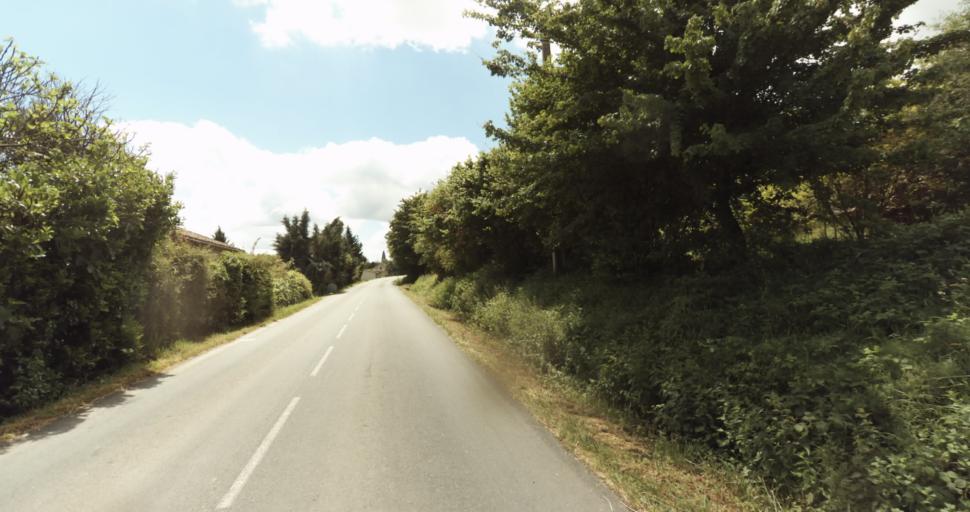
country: FR
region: Aquitaine
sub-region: Departement du Lot-et-Garonne
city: Villereal
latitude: 44.6967
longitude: 0.7511
